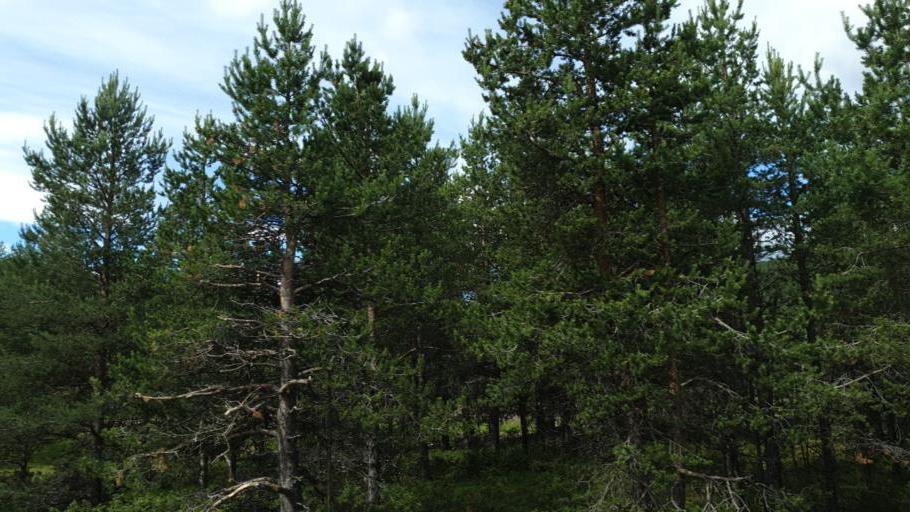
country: NO
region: Oppland
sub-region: Vaga
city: Vagamo
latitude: 61.7202
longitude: 9.0575
